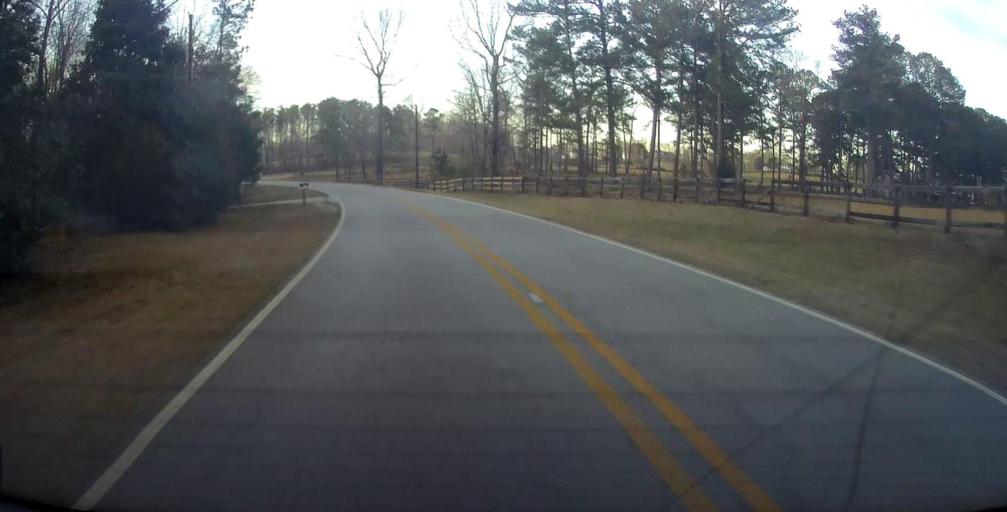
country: US
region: Georgia
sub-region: Harris County
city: Hamilton
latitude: 32.6012
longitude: -84.8783
